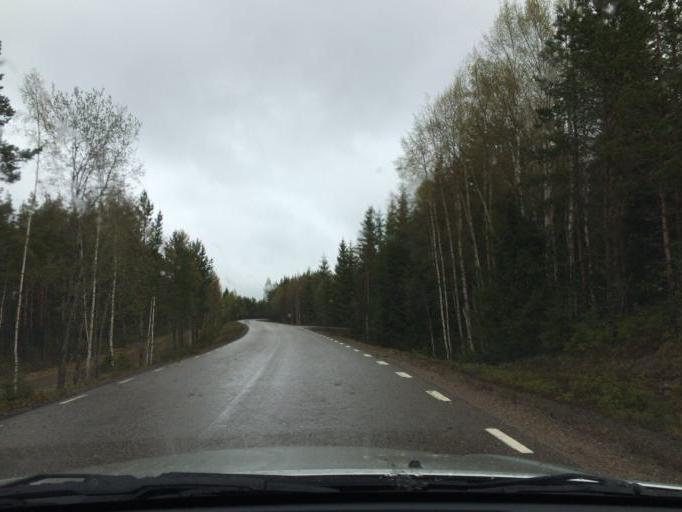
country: SE
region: Dalarna
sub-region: Ludvika Kommun
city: Abborrberget
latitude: 60.0619
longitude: 14.8095
